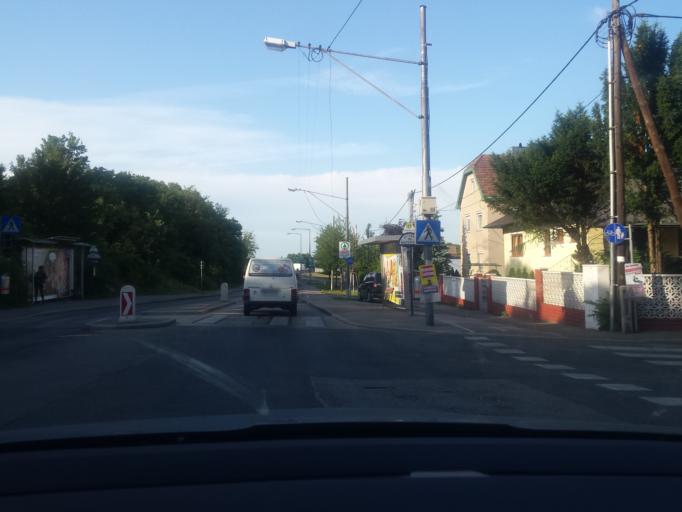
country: AT
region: Lower Austria
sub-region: Politischer Bezirk Wien-Umgebung
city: Leopoldsdorf
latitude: 48.1630
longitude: 16.4093
